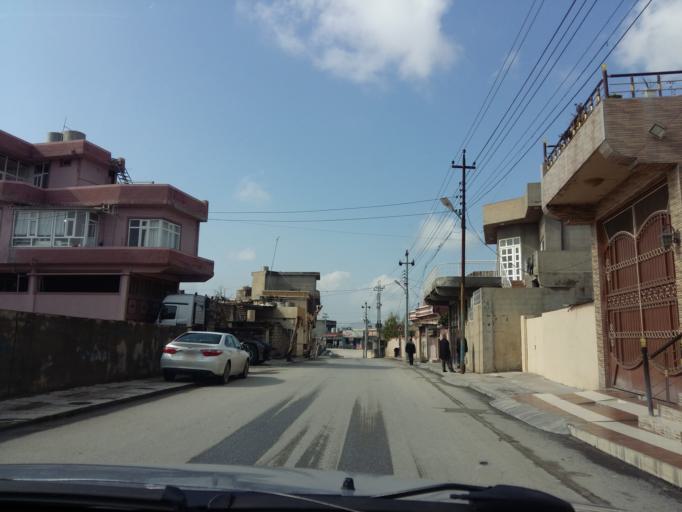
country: IQ
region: As Sulaymaniyah
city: Qeladize
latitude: 36.1862
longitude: 45.1193
